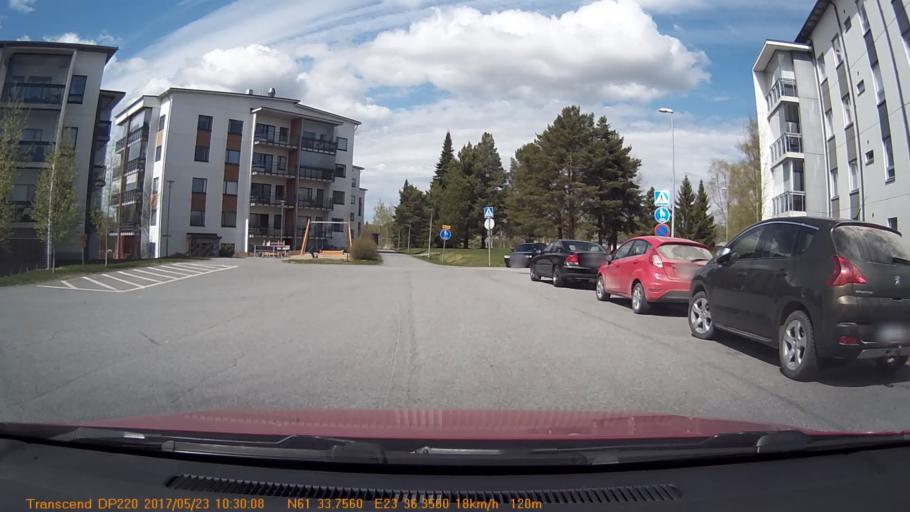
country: FI
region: Pirkanmaa
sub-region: Tampere
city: Yloejaervi
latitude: 61.5627
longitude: 23.6059
